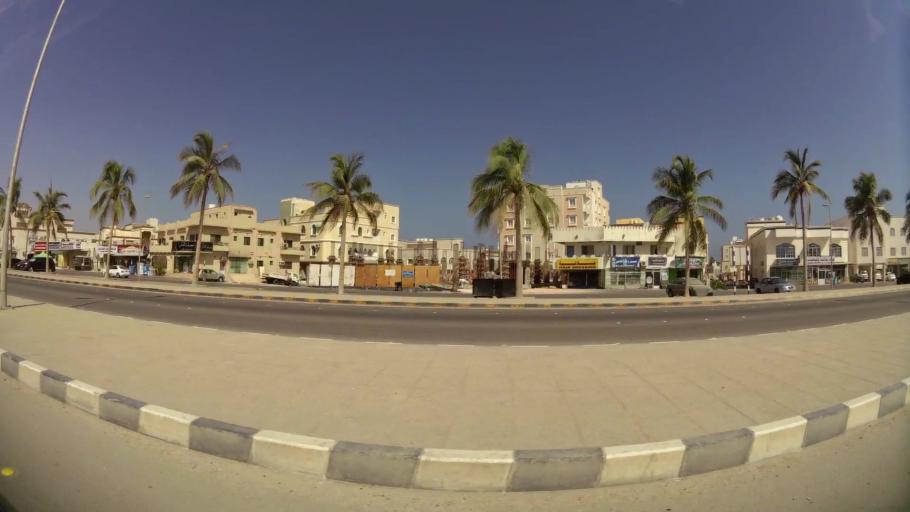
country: OM
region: Zufar
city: Salalah
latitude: 17.0016
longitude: 54.0370
